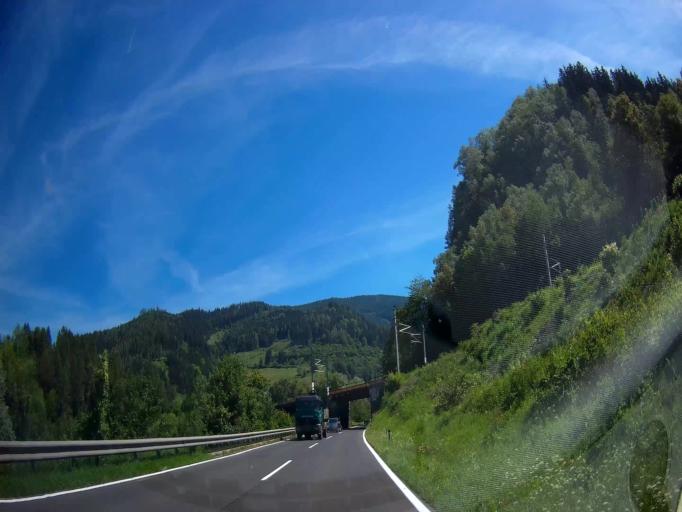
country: AT
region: Carinthia
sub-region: Politischer Bezirk Sankt Veit an der Glan
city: Micheldorf
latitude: 46.8918
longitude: 14.4423
